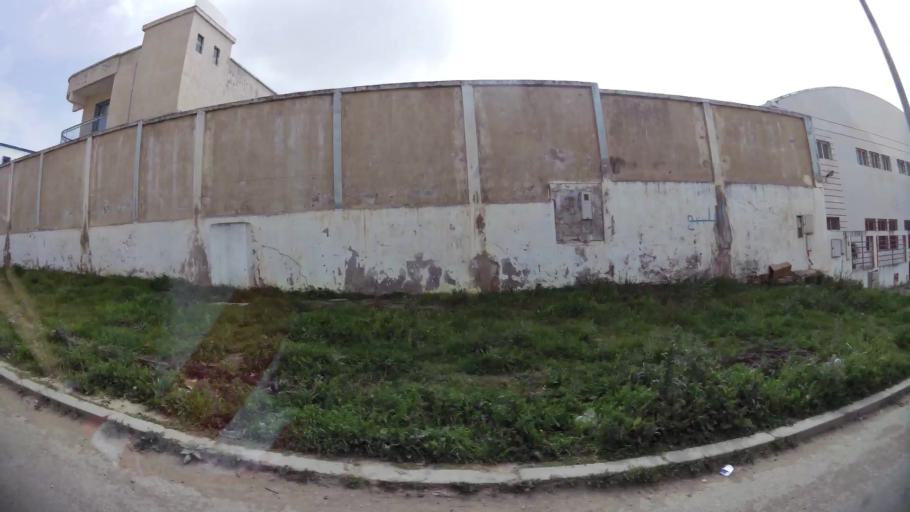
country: MA
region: Tanger-Tetouan
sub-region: Tanger-Assilah
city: Boukhalef
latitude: 35.7136
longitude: -5.8959
